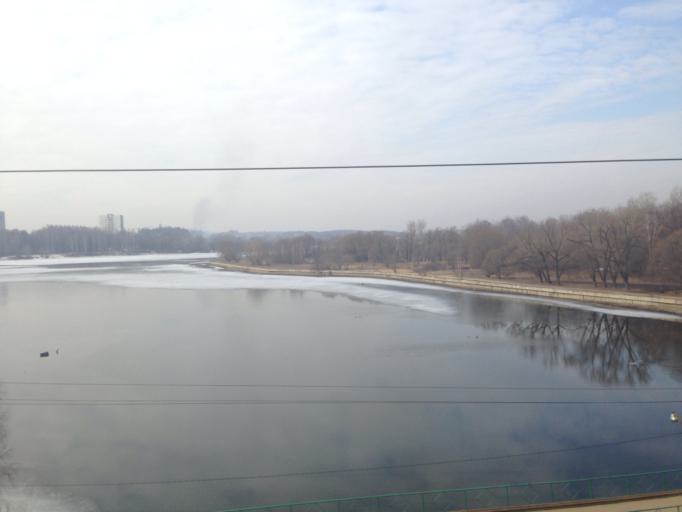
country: RU
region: Moskovskaya
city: Dolgoprudnyy
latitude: 55.9570
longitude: 37.5094
